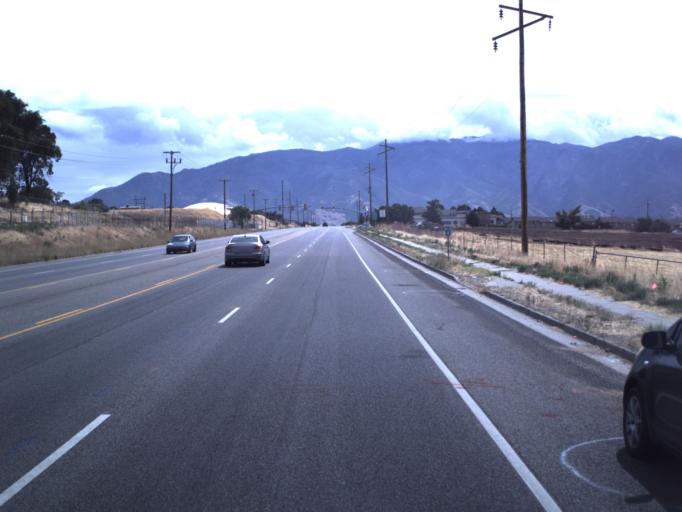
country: US
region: Utah
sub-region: Davis County
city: Hill Air Force Bace
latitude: 41.1035
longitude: -111.9925
